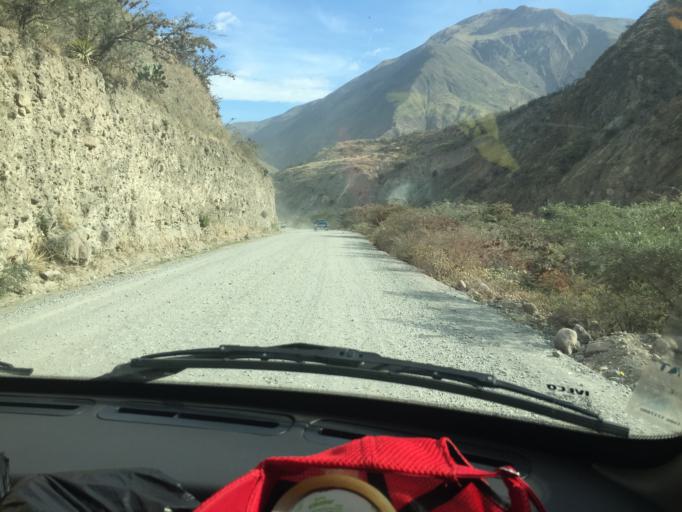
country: EC
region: Carchi
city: El Angel
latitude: 0.6032
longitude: -78.1382
